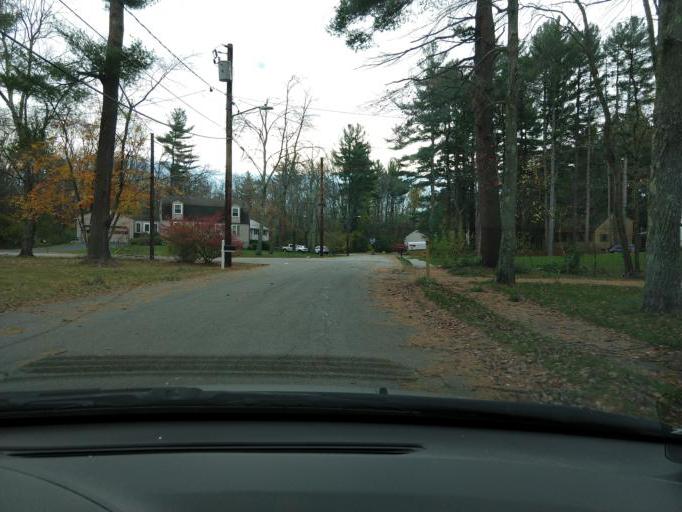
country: US
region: Massachusetts
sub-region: Middlesex County
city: Bedford
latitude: 42.4876
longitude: -71.2926
